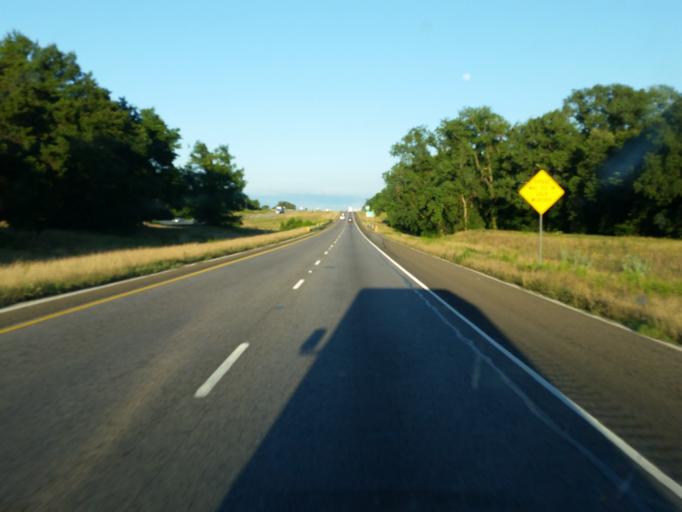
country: US
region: Texas
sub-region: Van Zandt County
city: Wills Point
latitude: 32.6616
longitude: -96.1190
